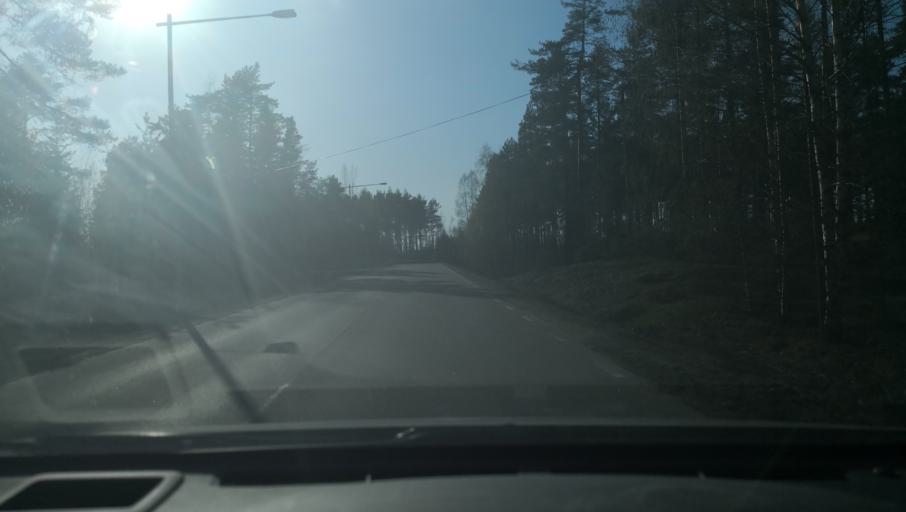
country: SE
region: Uppsala
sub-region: Heby Kommun
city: Tarnsjo
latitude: 60.1544
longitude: 16.9368
